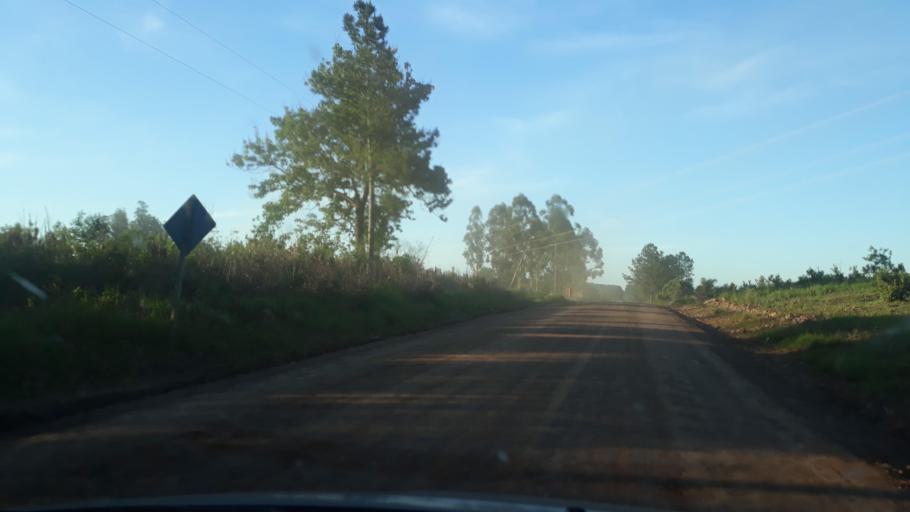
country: AR
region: Misiones
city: Ruiz de Montoya
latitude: -27.0522
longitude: -55.0043
